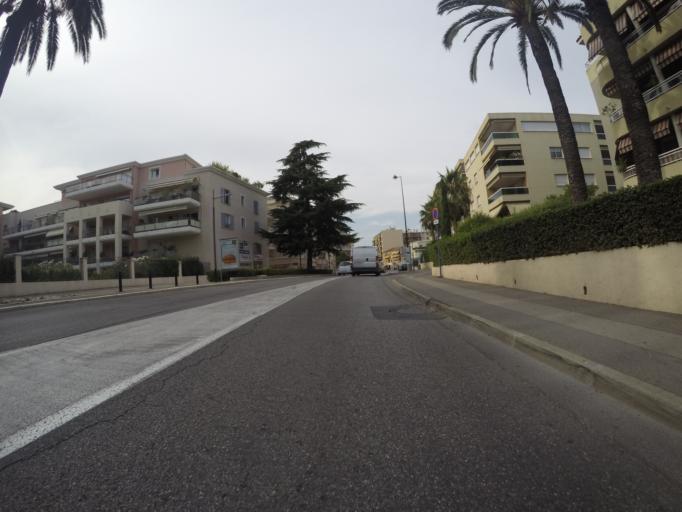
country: FR
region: Provence-Alpes-Cote d'Azur
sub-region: Departement des Alpes-Maritimes
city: Cagnes-sur-Mer
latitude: 43.6633
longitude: 7.1547
